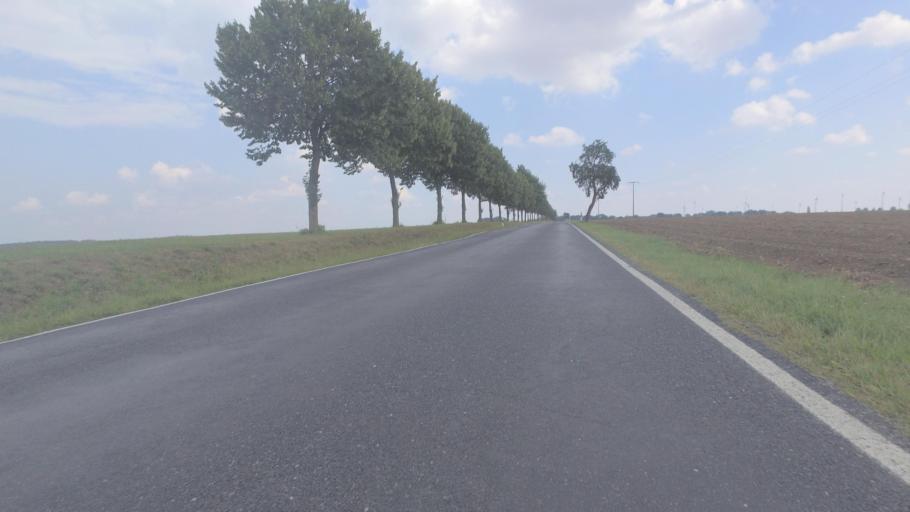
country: DE
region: Mecklenburg-Vorpommern
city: Borrentin
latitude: 53.8506
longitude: 12.9822
